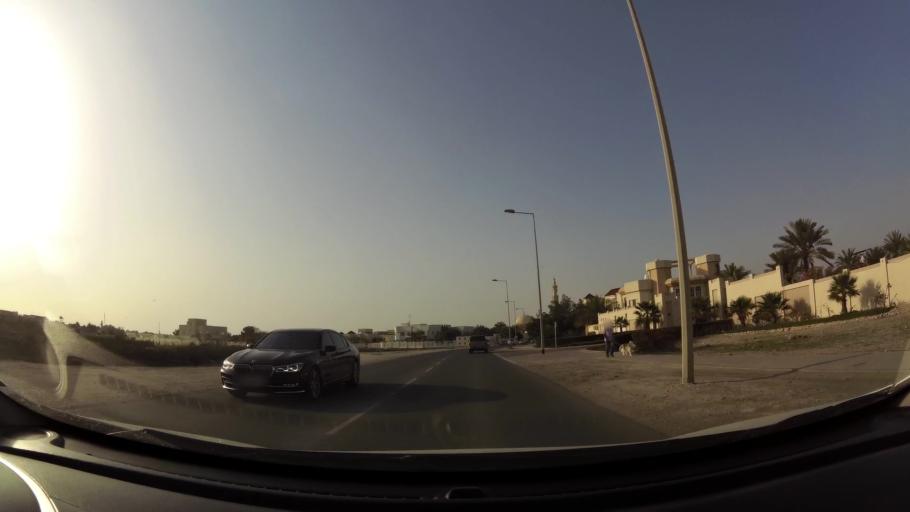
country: BH
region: Manama
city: Jidd Hafs
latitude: 26.2101
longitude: 50.4812
